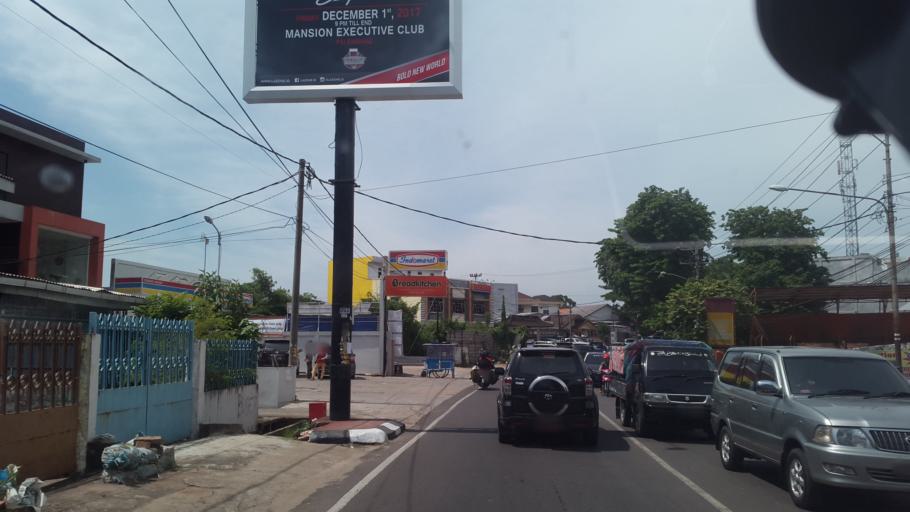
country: ID
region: South Sumatra
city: Plaju
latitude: -2.9892
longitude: 104.7383
